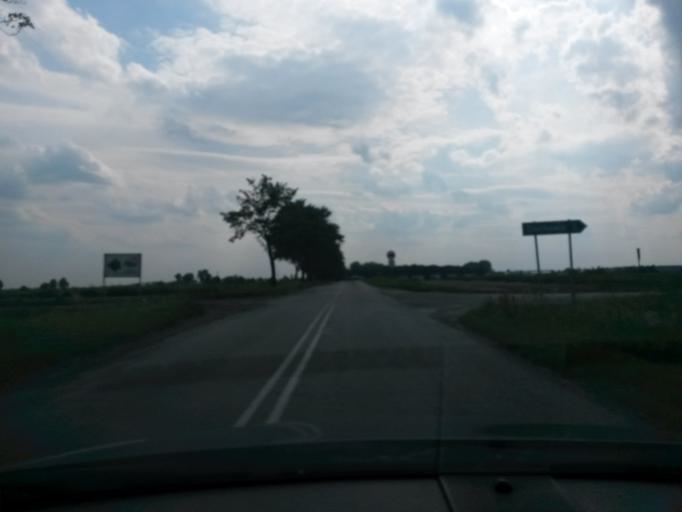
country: PL
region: Greater Poland Voivodeship
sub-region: Powiat poznanski
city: Kornik
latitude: 52.2893
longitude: 17.1148
